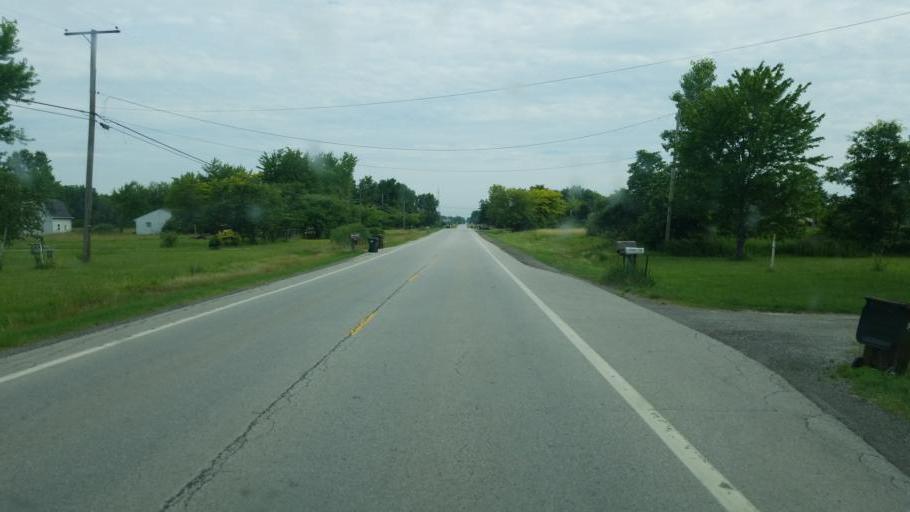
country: US
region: Ohio
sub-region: Lorain County
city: Grafton
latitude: 41.2152
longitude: -82.0236
